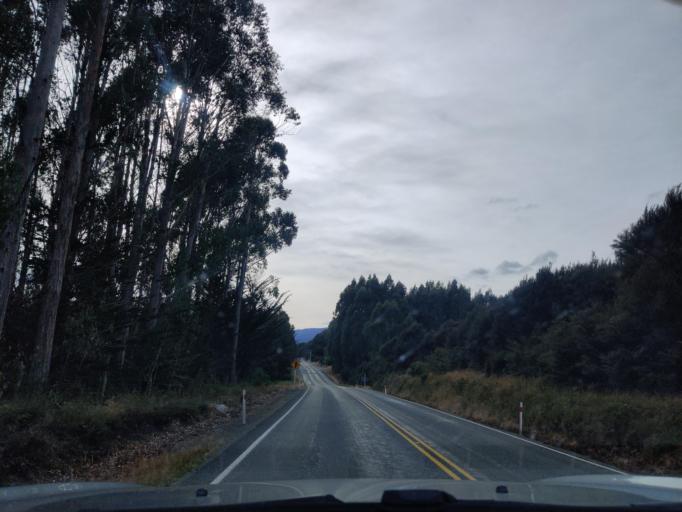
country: NZ
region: Tasman
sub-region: Tasman District
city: Wakefield
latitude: -41.7776
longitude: 172.9159
